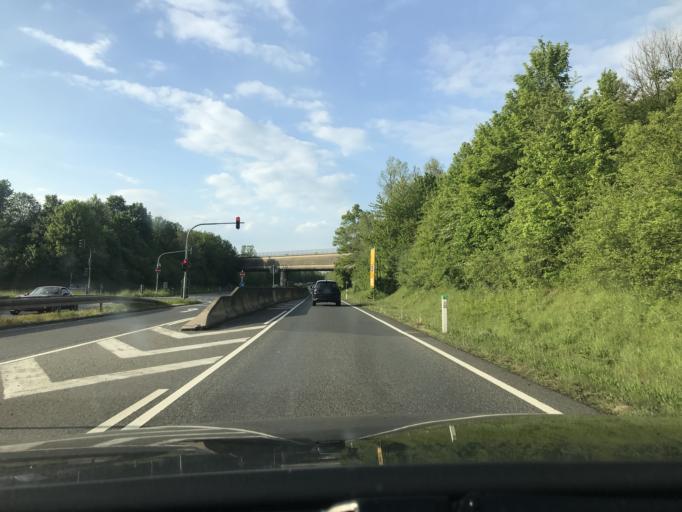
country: DE
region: North Rhine-Westphalia
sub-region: Regierungsbezirk Koln
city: Erftstadt
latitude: 50.8106
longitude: 6.8065
